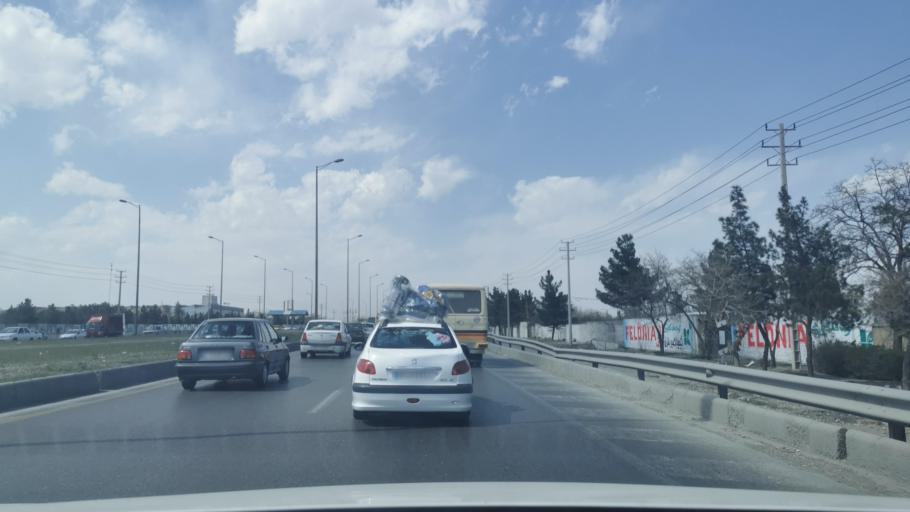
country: IR
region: Razavi Khorasan
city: Torqabeh
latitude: 36.4335
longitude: 59.4490
